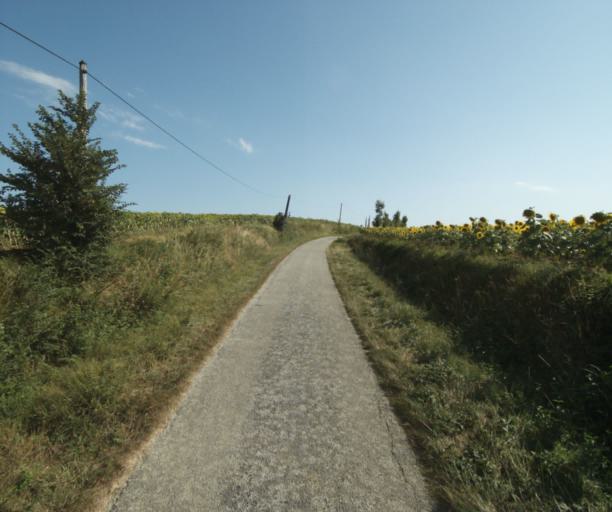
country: FR
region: Midi-Pyrenees
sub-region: Departement de la Haute-Garonne
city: Avignonet-Lauragais
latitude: 43.4216
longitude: 1.8173
